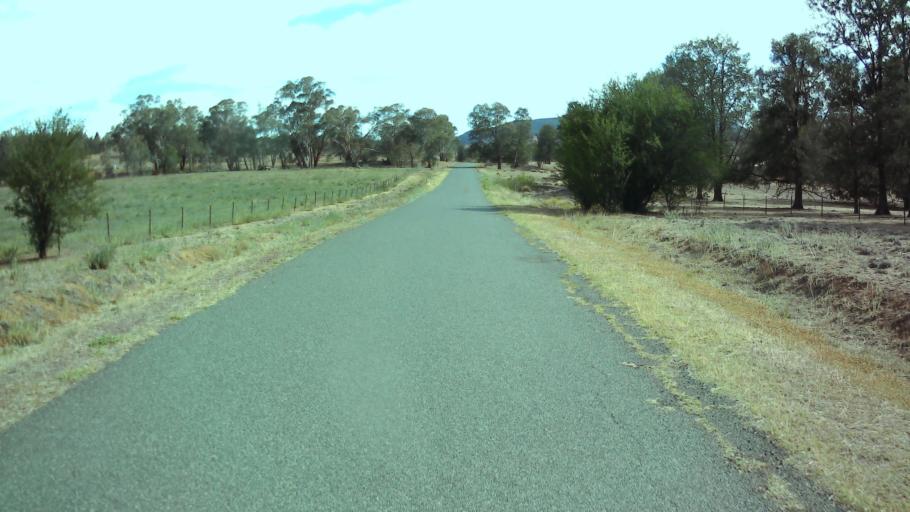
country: AU
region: New South Wales
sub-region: Weddin
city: Grenfell
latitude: -33.8133
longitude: 148.2922
